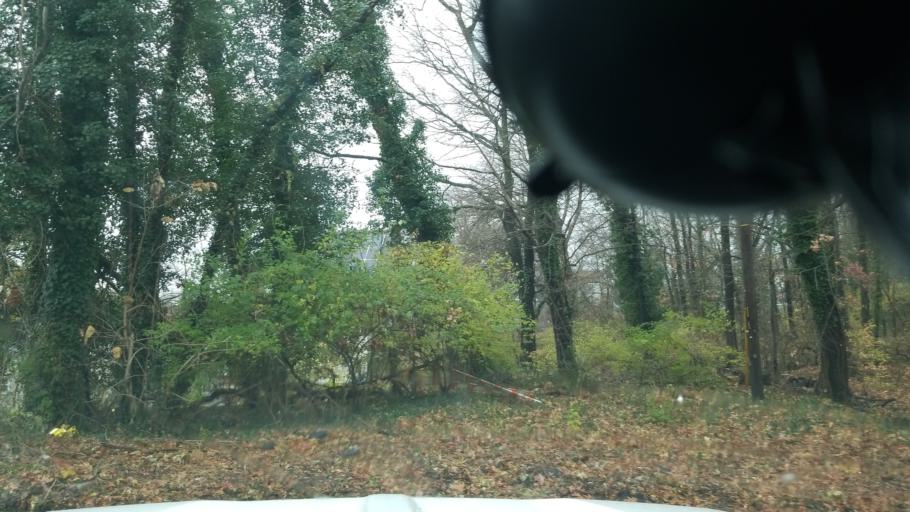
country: US
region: Maryland
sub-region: Prince George's County
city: Mount Rainier
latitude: 38.9231
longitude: -76.9756
